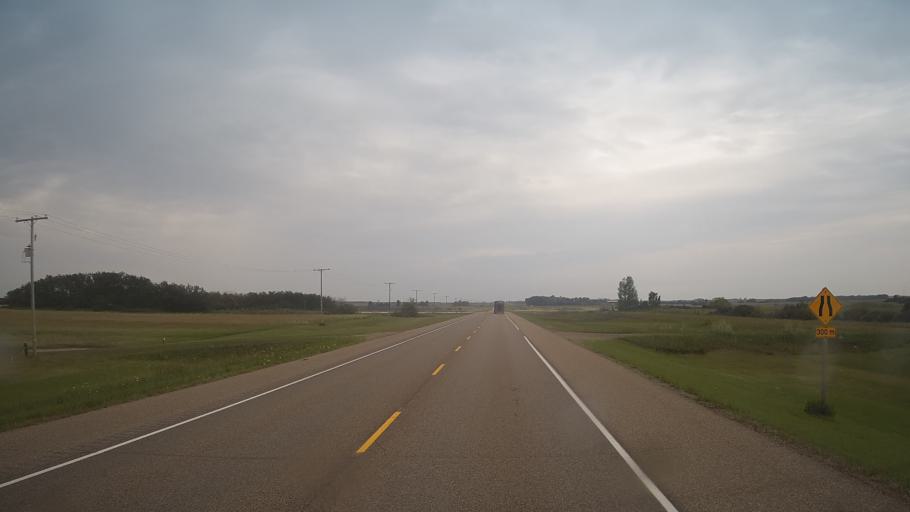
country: CA
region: Saskatchewan
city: Langham
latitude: 52.1289
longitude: -107.1215
